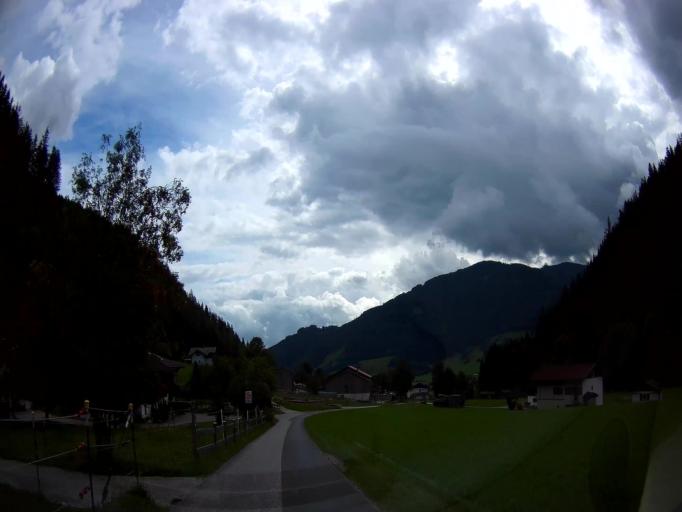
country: AT
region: Salzburg
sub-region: Politischer Bezirk Zell am See
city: Leogang
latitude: 47.4494
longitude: 12.7645
